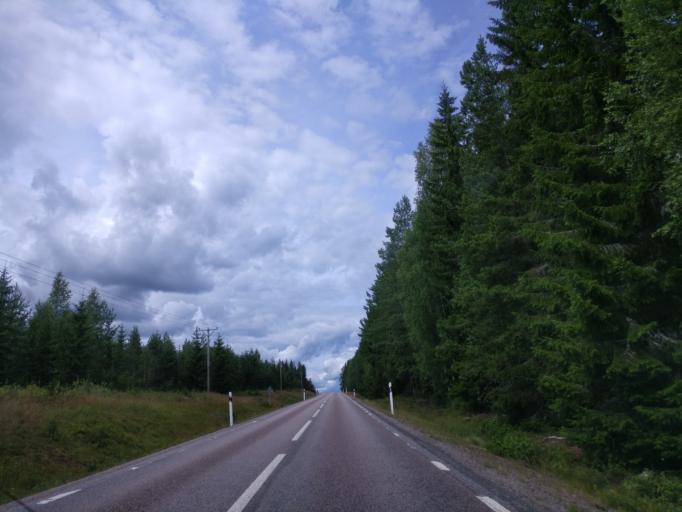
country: SE
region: Vaermland
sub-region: Hagfors Kommun
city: Ekshaerad
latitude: 60.1802
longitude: 13.3535
